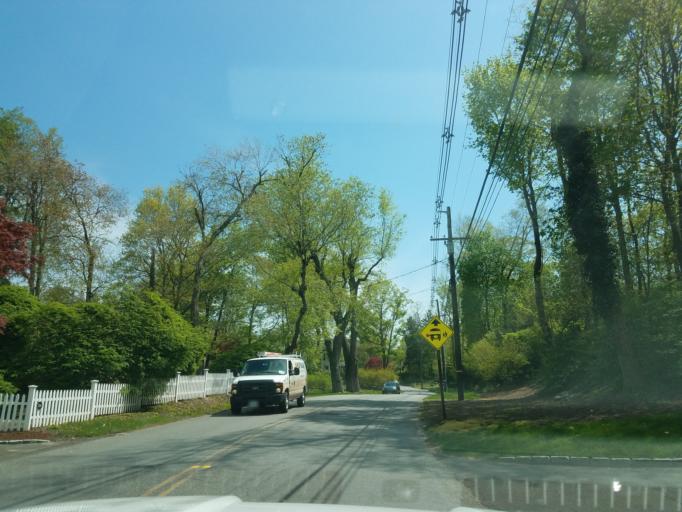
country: US
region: Connecticut
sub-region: Fairfield County
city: New Canaan
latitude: 41.1265
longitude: -73.4744
